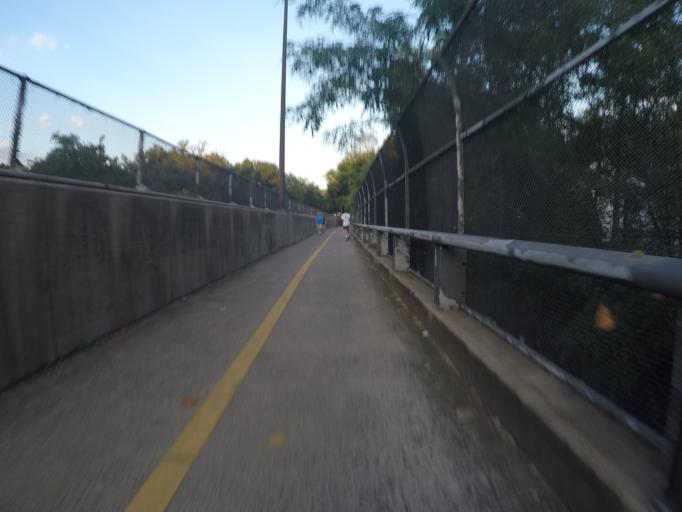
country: US
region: Virginia
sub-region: Arlington County
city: Arlington
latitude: 38.8976
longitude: -77.0940
